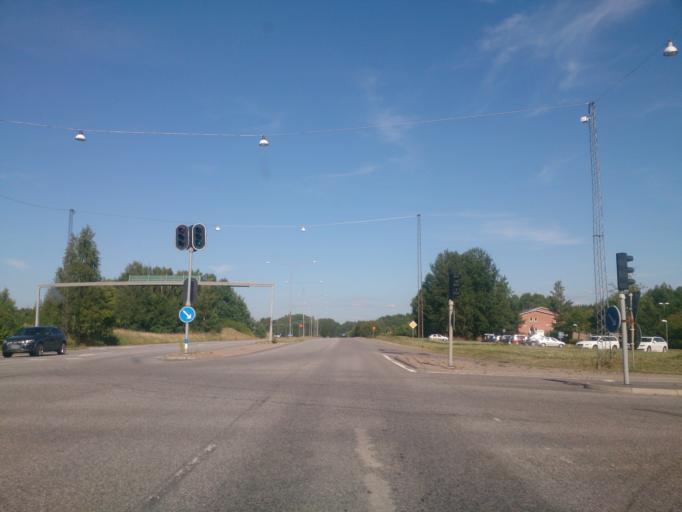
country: SE
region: OEstergoetland
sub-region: Norrkopings Kommun
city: Norrkoping
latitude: 58.5648
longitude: 16.1732
